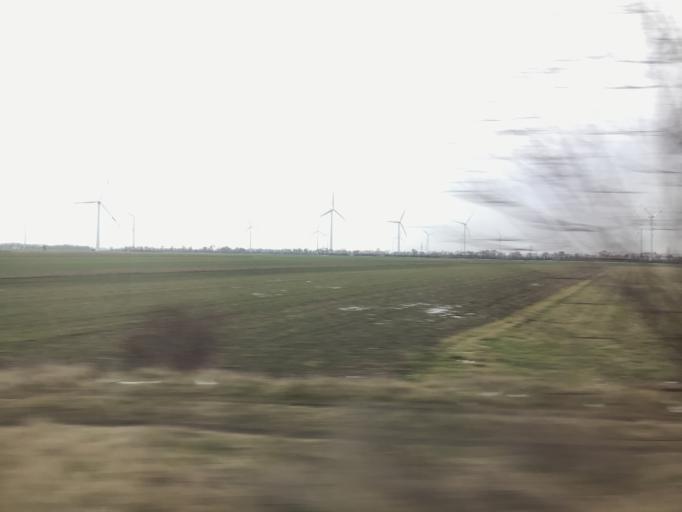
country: AT
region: Burgenland
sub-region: Politischer Bezirk Neusiedl am See
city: Parndorf
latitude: 47.9872
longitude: 16.8802
